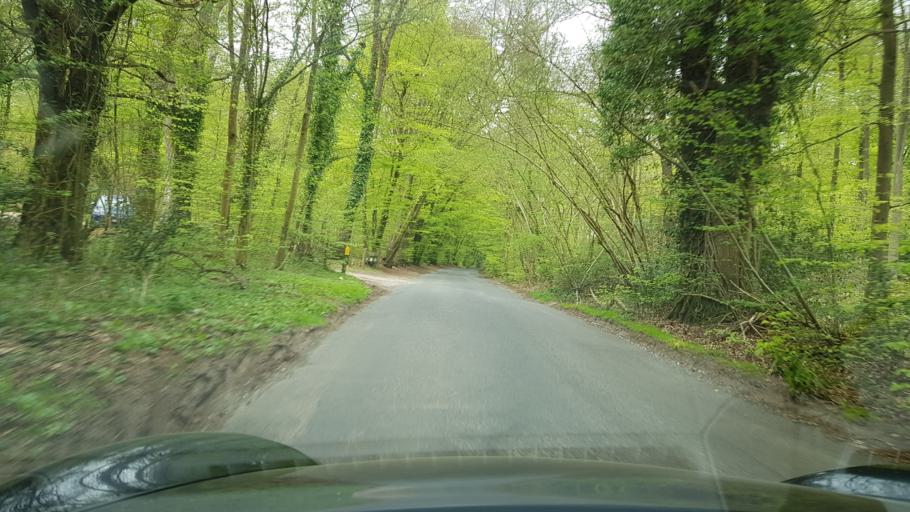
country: GB
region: England
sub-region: Surrey
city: East Horsley
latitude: 51.2329
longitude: -0.4038
